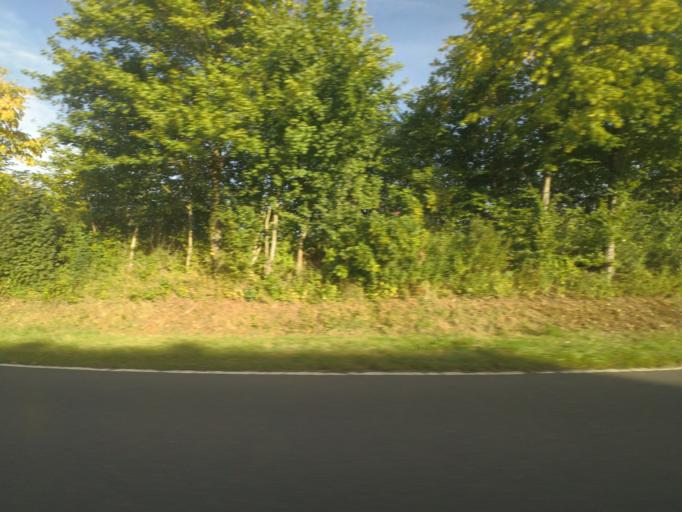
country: DE
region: Hesse
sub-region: Regierungsbezirk Kassel
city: Flieden
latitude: 50.4463
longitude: 9.5791
